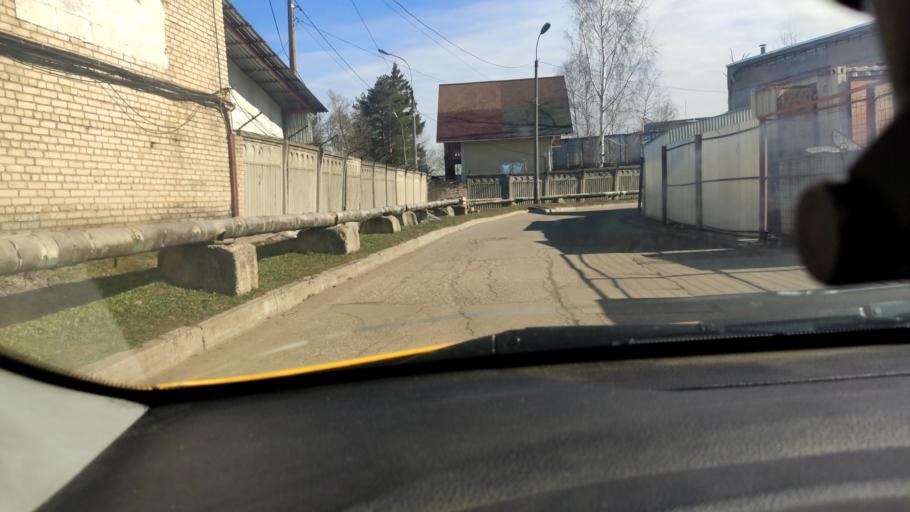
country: RU
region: Moskovskaya
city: Selyatino
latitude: 55.5143
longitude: 36.9664
